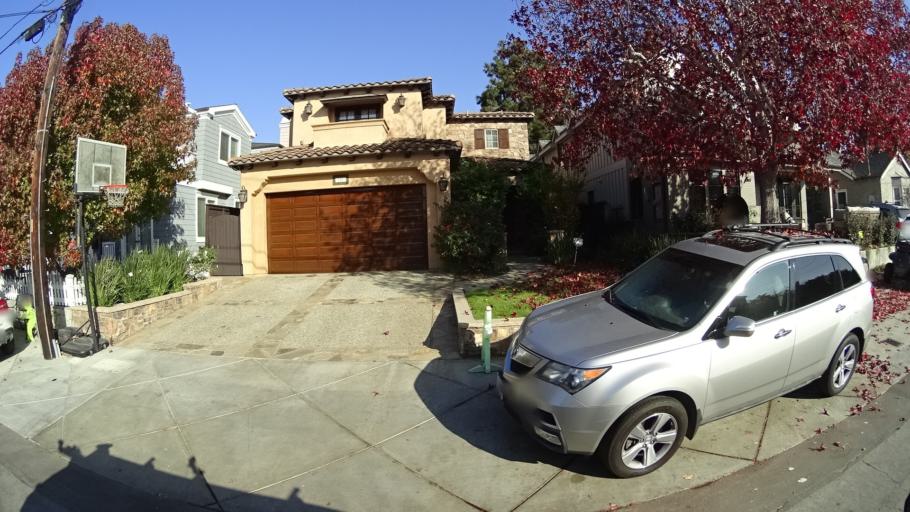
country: US
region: California
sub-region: Los Angeles County
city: Manhattan Beach
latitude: 33.8971
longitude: -118.4082
